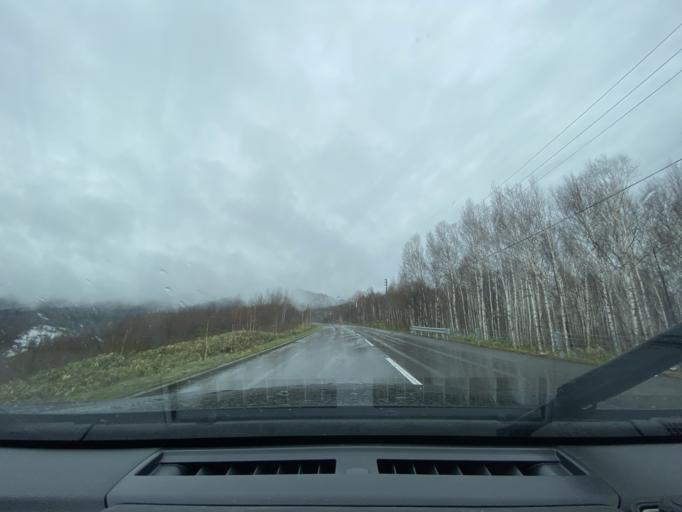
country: JP
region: Hokkaido
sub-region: Asahikawa-shi
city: Asahikawa
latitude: 43.8175
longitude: 142.2548
